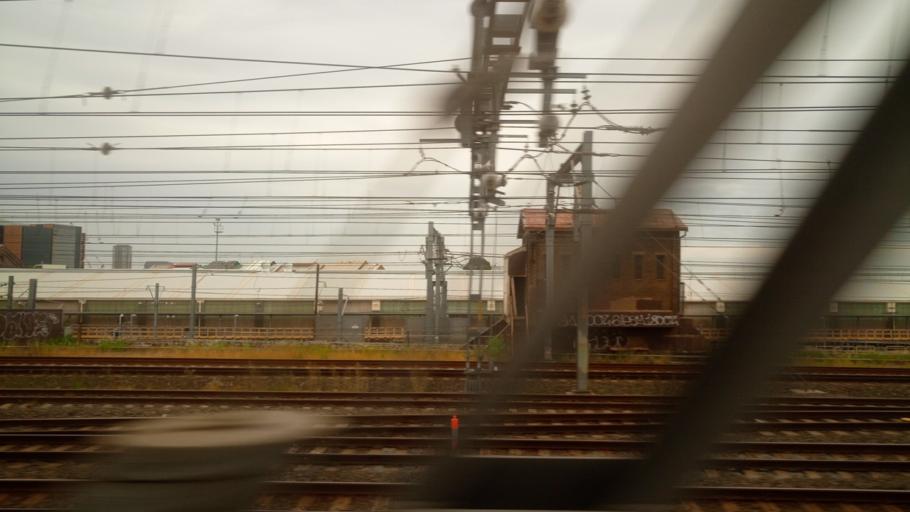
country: AU
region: New South Wales
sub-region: City of Sydney
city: Darlington
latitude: -33.8952
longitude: 151.1905
